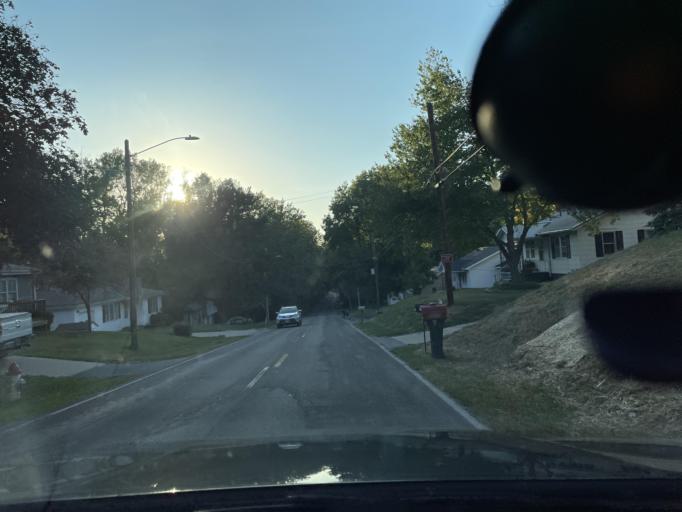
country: US
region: Missouri
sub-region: Andrew County
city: Country Club Village
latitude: 39.7994
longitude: -94.8261
